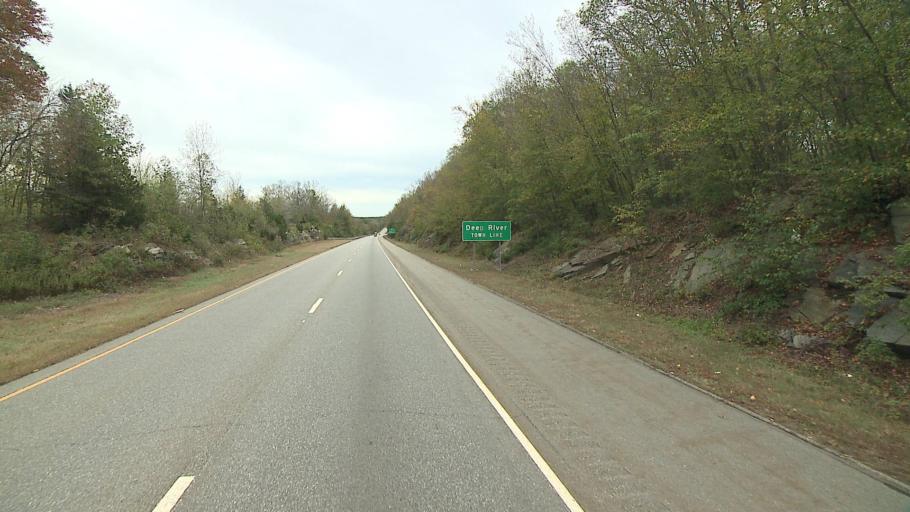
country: US
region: Connecticut
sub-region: Middlesex County
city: Chester Center
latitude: 41.3879
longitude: -72.4553
